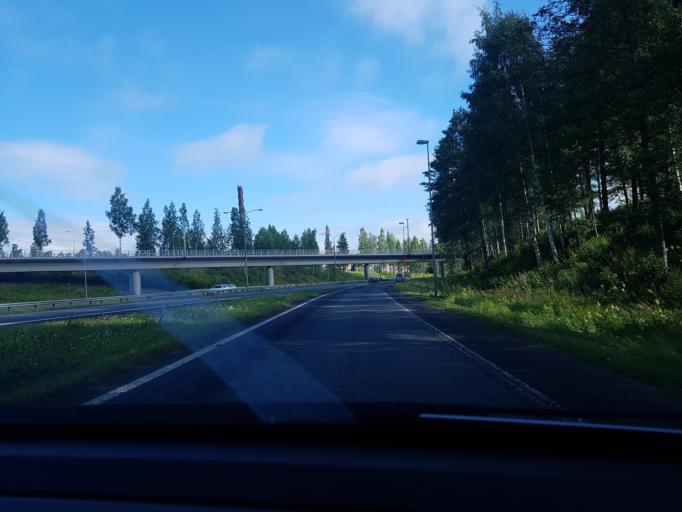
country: FI
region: Northern Savo
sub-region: Kuopio
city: Kuopio
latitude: 62.8867
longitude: 27.6372
